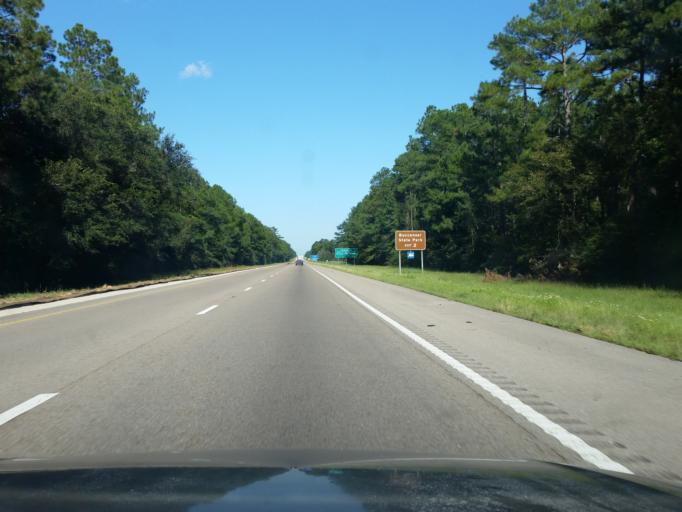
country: US
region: Mississippi
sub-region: Hancock County
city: Pearlington
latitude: 30.3113
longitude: -89.6114
